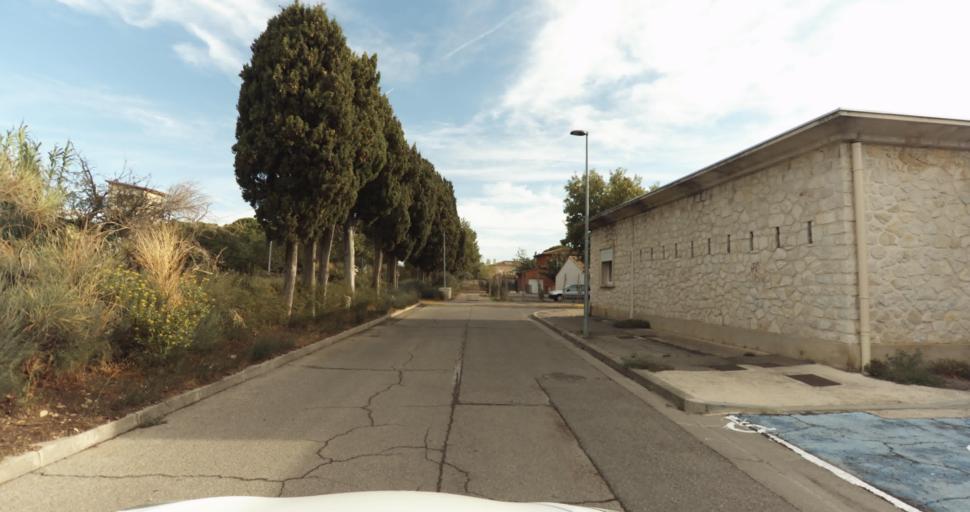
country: FR
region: Provence-Alpes-Cote d'Azur
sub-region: Departement des Bouches-du-Rhone
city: Miramas
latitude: 43.5874
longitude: 4.9973
